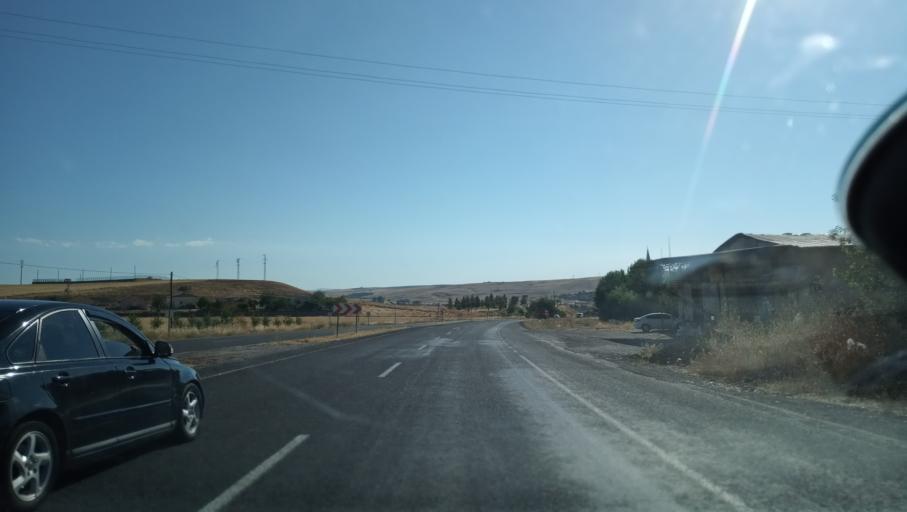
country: TR
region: Diyarbakir
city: Sur
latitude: 37.9892
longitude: 40.3738
